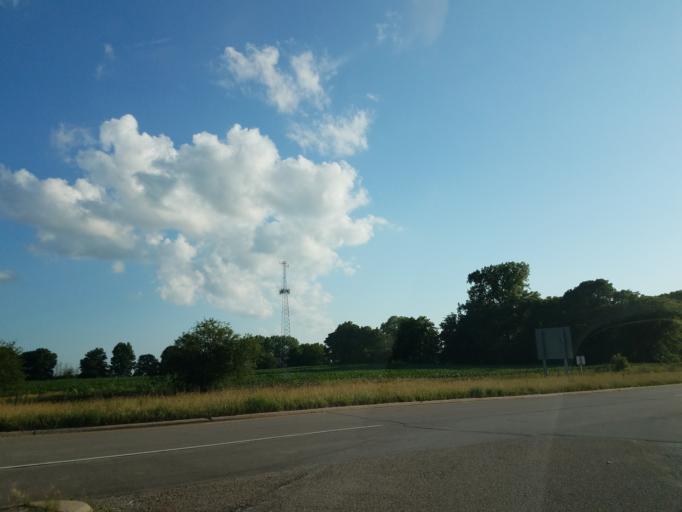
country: US
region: Illinois
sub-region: McLean County
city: Twin Grove
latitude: 40.4085
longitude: -89.0567
